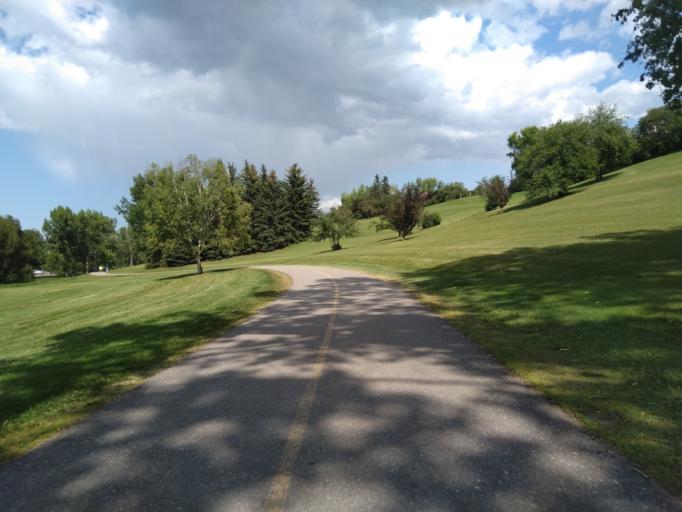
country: CA
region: Alberta
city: Calgary
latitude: 51.0774
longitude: -114.0808
